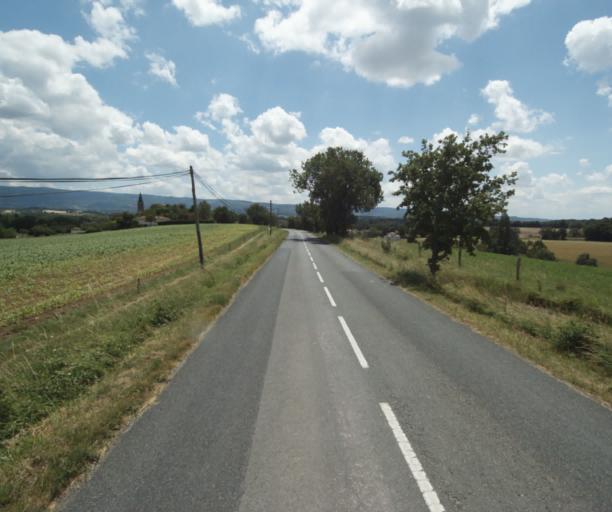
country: FR
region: Midi-Pyrenees
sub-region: Departement du Tarn
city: Soual
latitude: 43.5325
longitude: 2.0618
